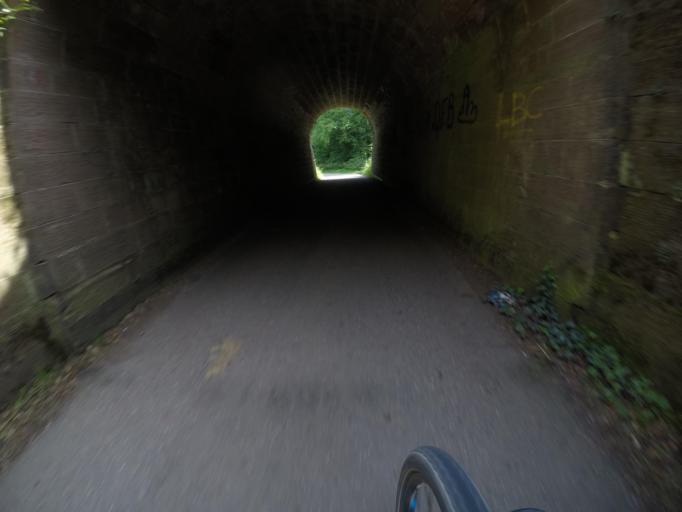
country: DE
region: Baden-Wuerttemberg
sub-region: Karlsruhe Region
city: Otisheim
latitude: 48.9719
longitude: 8.8020
